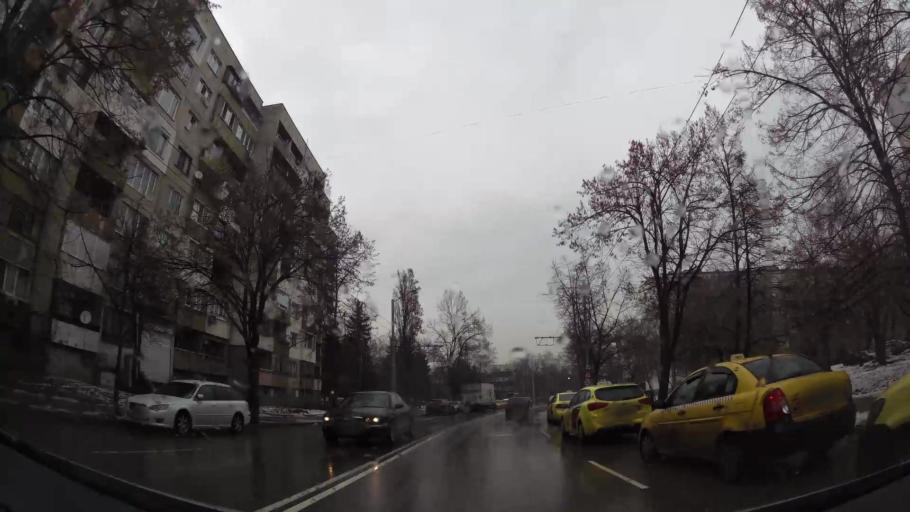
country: BG
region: Sofia-Capital
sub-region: Stolichna Obshtina
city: Sofia
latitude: 42.6633
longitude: 23.2964
